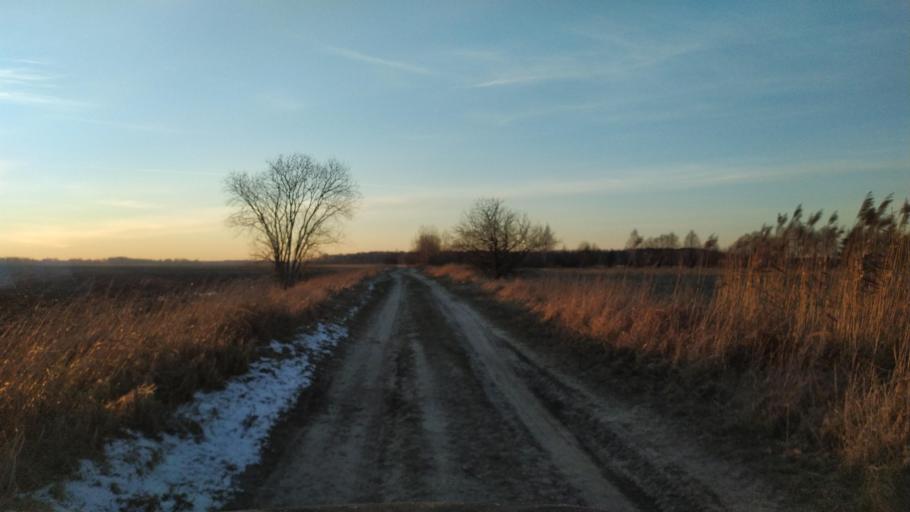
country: BY
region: Brest
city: Pruzhany
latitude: 52.5538
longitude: 24.2637
